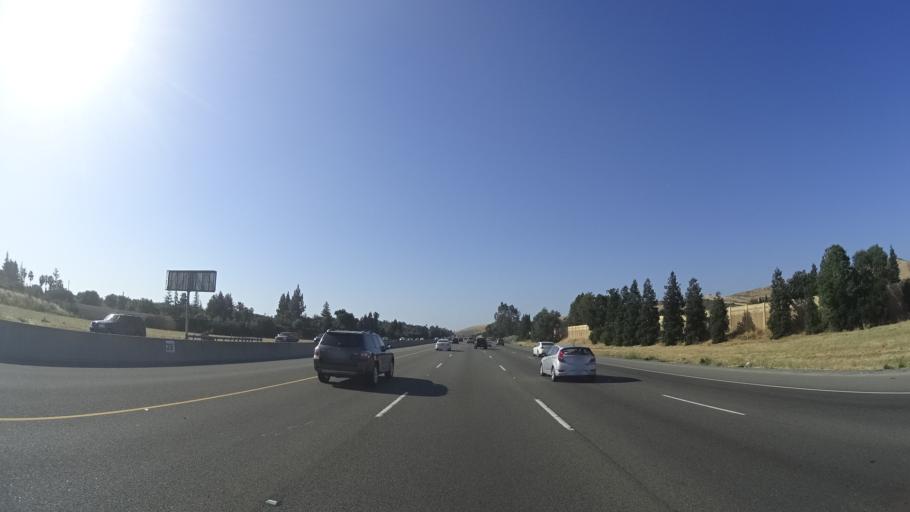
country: US
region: California
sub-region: Santa Clara County
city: Seven Trees
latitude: 37.2664
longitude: -121.8017
